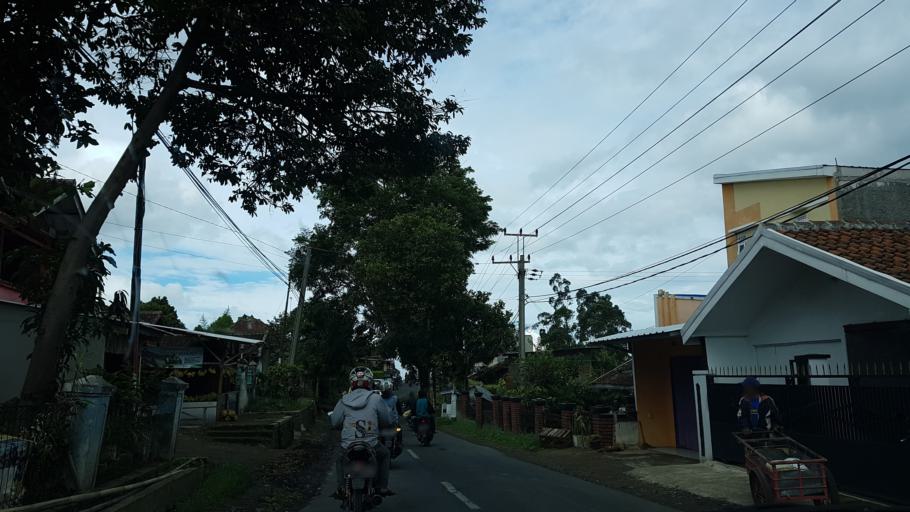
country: ID
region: West Java
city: Banjar
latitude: -7.1107
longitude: 107.4510
